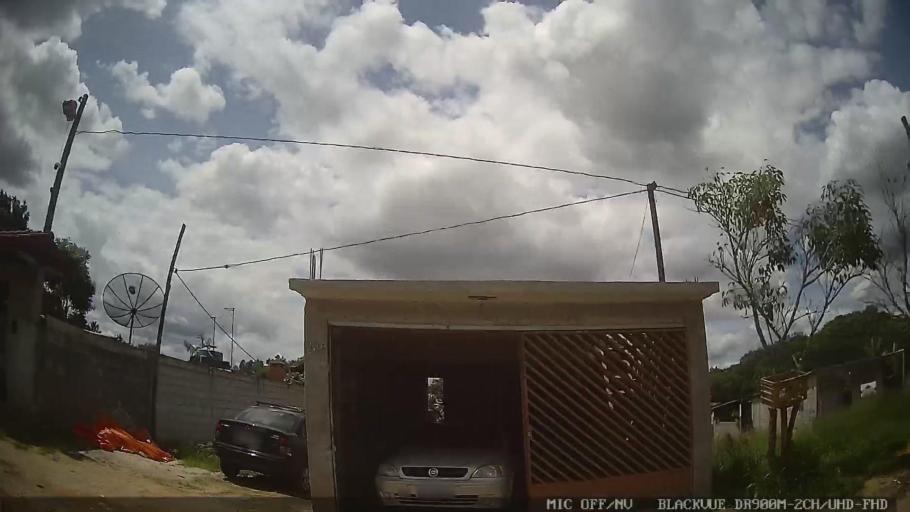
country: BR
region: Sao Paulo
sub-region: Mogi das Cruzes
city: Mogi das Cruzes
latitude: -23.6097
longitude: -46.2359
